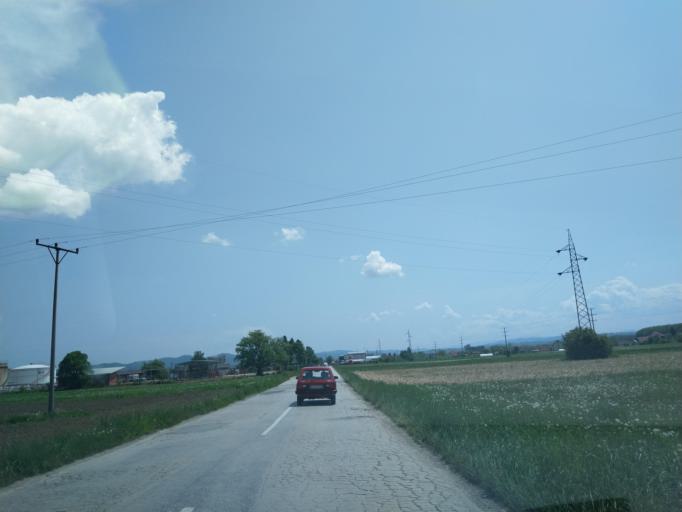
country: RS
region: Central Serbia
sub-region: Zlatiborski Okrug
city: Pozega
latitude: 43.8498
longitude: 20.0080
